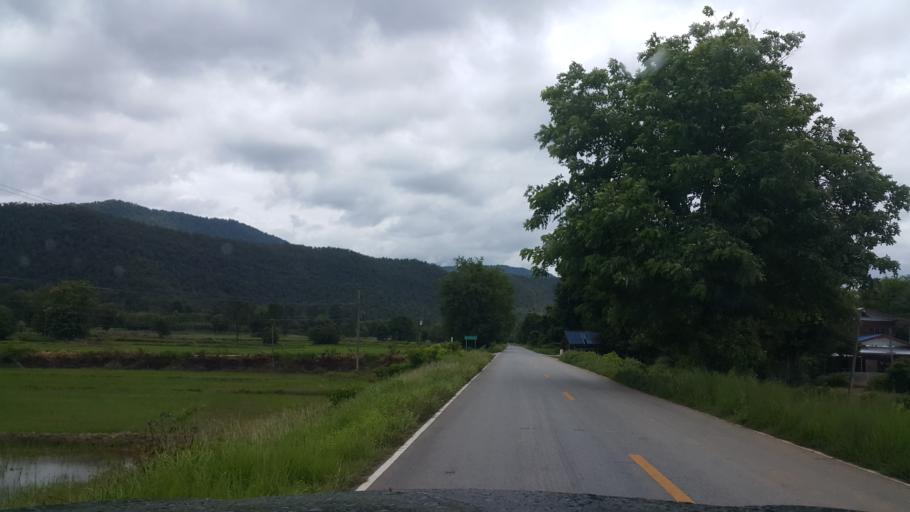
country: TH
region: Phitsanulok
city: Chat Trakan
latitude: 17.3068
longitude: 100.6693
